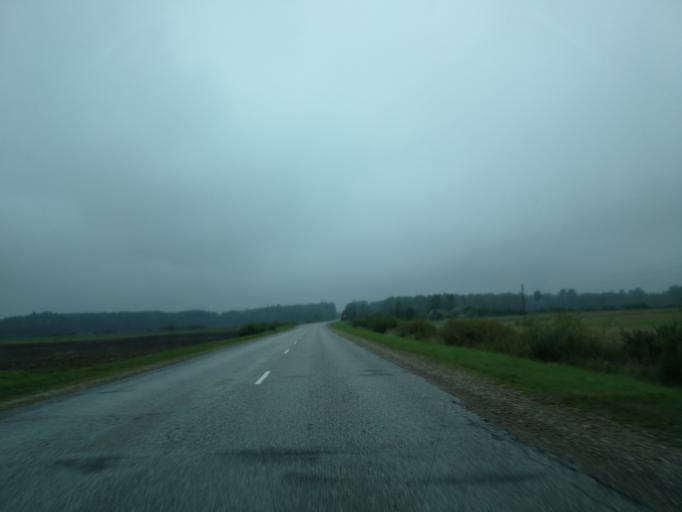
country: LV
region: Varkava
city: Vecvarkava
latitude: 56.3146
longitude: 26.5022
